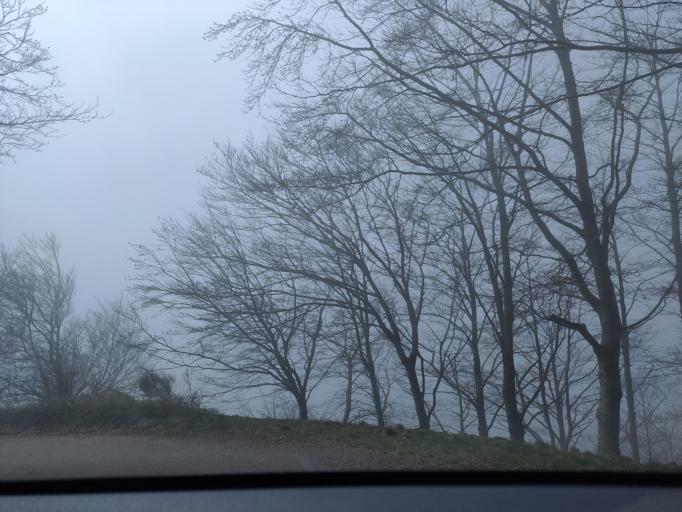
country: ES
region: Catalonia
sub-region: Provincia de Barcelona
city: Fogars de Montclus
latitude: 41.7596
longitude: 2.4554
